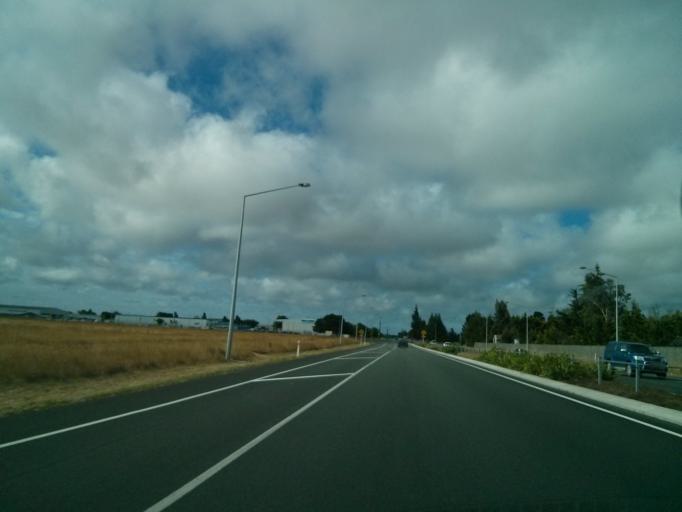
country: NZ
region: Canterbury
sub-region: Selwyn District
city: Prebbleton
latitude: -43.4995
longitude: 172.5462
